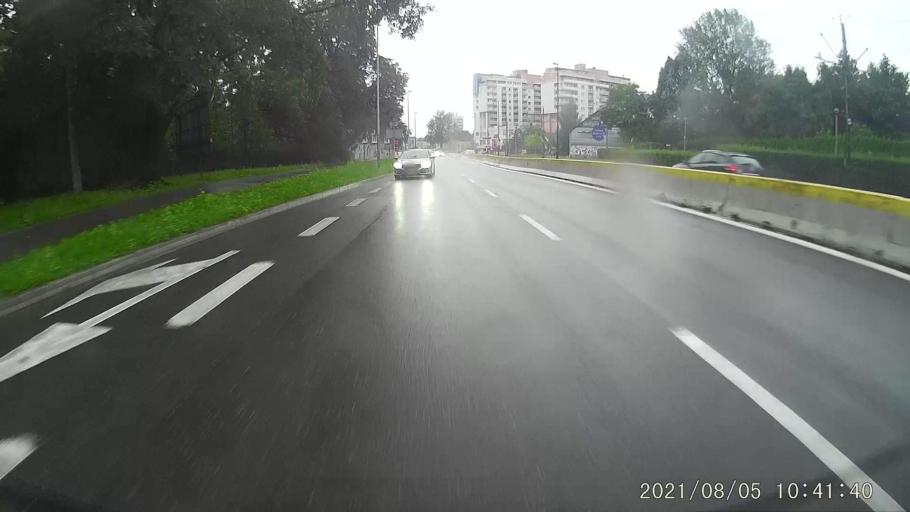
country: PL
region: Lesser Poland Voivodeship
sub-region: Krakow
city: Krakow
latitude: 50.0371
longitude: 19.9256
